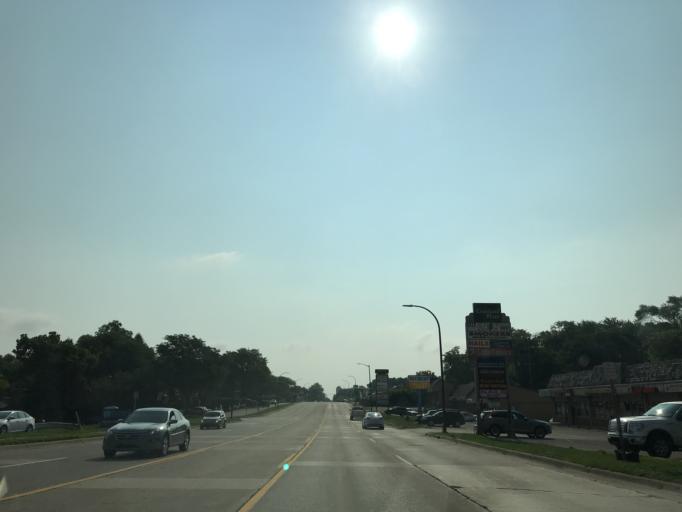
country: US
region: Michigan
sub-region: Washtenaw County
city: Ypsilanti
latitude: 42.2479
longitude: -83.6424
